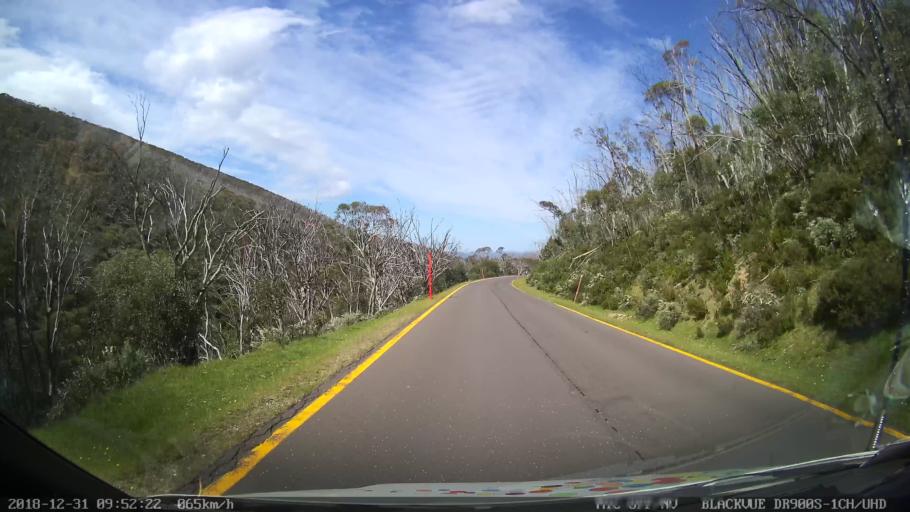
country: AU
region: New South Wales
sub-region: Snowy River
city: Jindabyne
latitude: -36.5269
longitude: 148.2539
